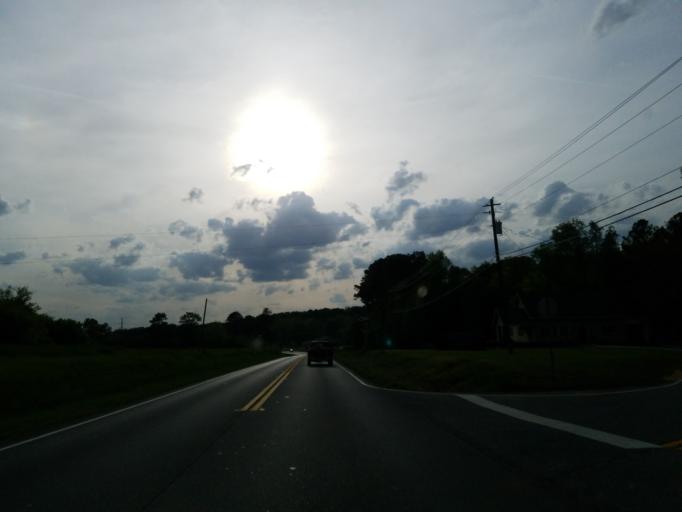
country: US
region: Georgia
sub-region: Cherokee County
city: Canton
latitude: 34.2418
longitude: -84.4015
